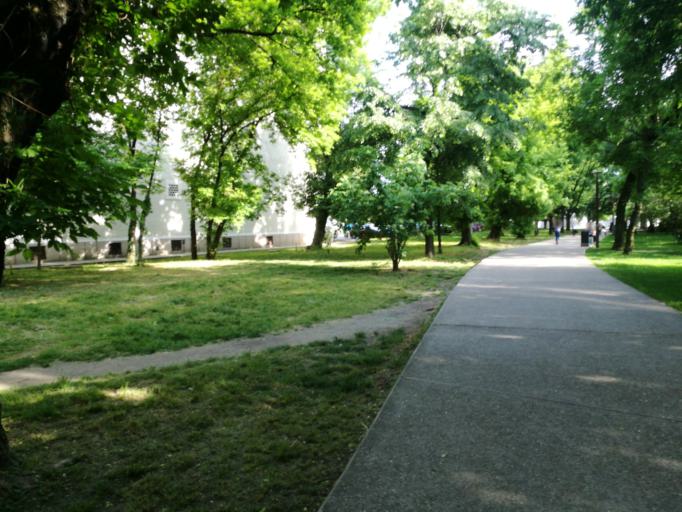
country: RO
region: Bucuresti
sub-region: Municipiul Bucuresti
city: Bucuresti
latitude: 44.4365
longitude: 26.0784
